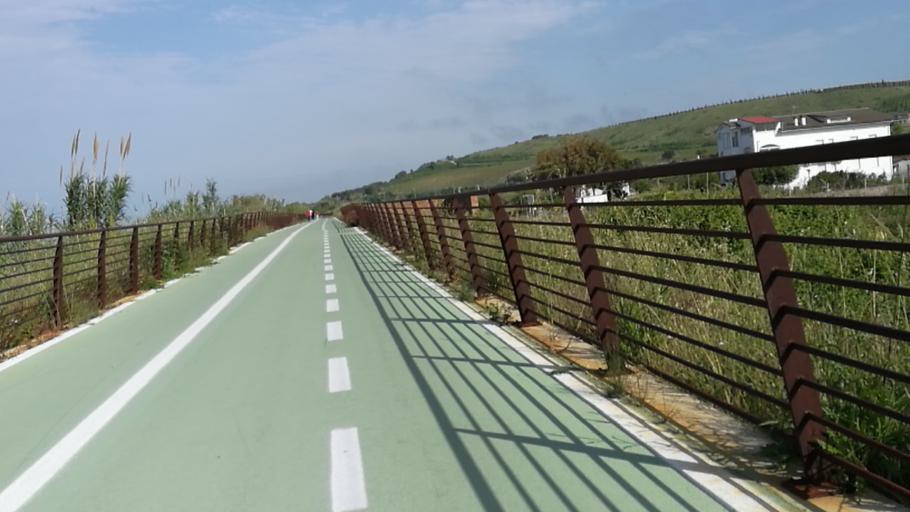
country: IT
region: Abruzzo
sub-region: Provincia di Chieti
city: Casalbordino-Miracoli
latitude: 42.2041
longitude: 14.6049
